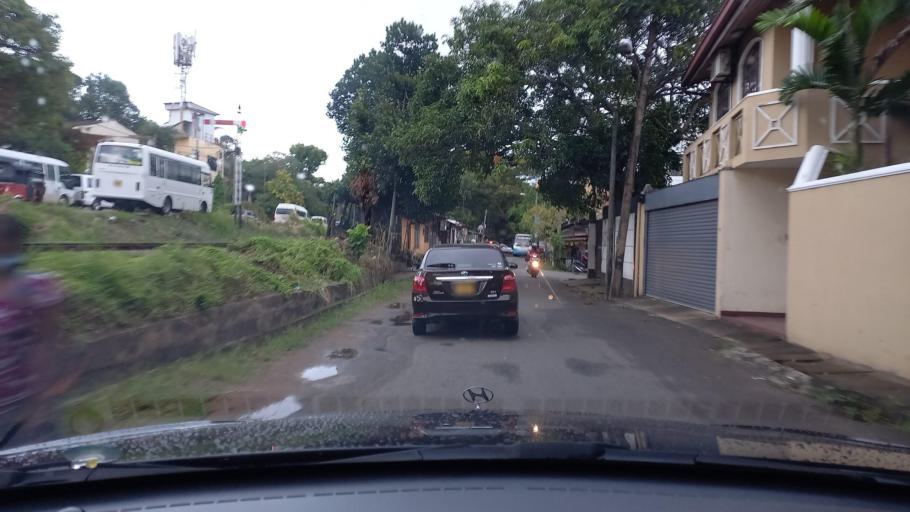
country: LK
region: Western
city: Sri Jayewardenepura Kotte
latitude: 6.8737
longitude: 79.8869
